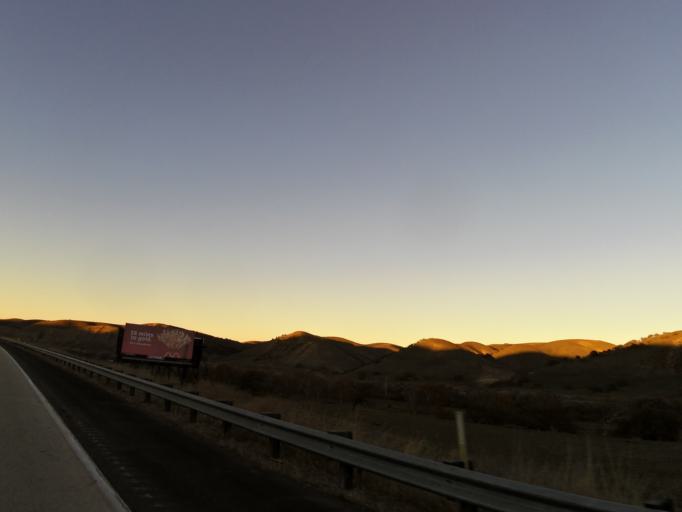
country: US
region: California
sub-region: San Luis Obispo County
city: Lake Nacimiento
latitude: 35.9019
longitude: -120.8426
